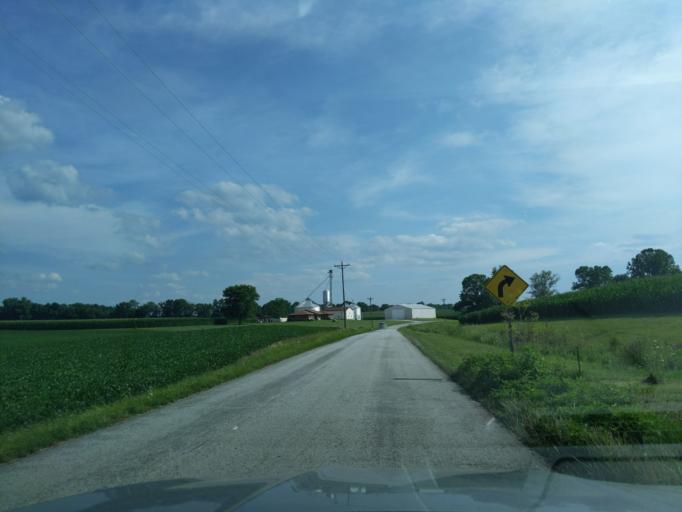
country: US
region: Indiana
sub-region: Decatur County
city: Greensburg
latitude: 39.2615
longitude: -85.4657
